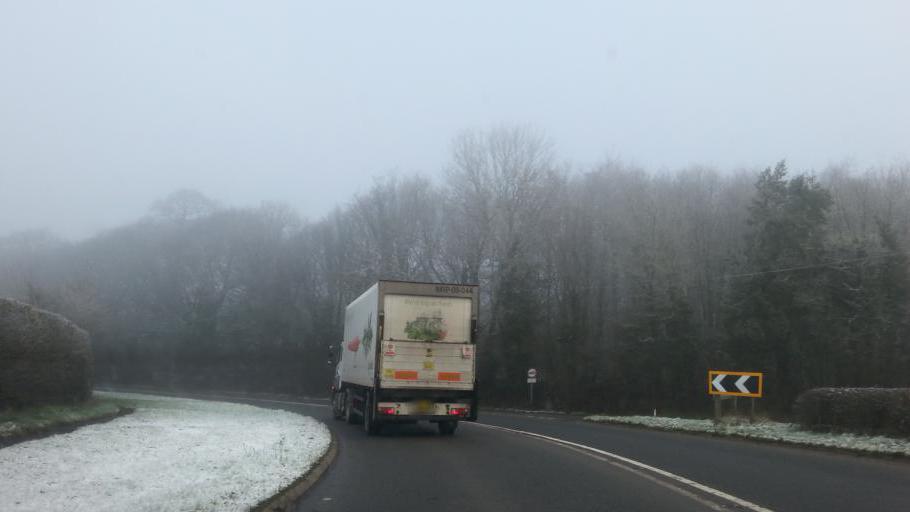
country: GB
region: England
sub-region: Cheshire East
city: Eaton
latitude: 53.1819
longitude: -2.2098
